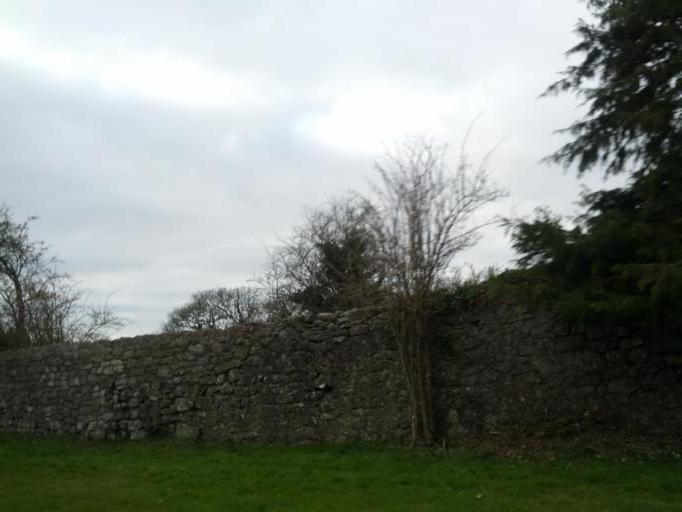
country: IE
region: Connaught
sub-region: County Galway
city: Oranmore
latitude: 53.2085
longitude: -8.8783
